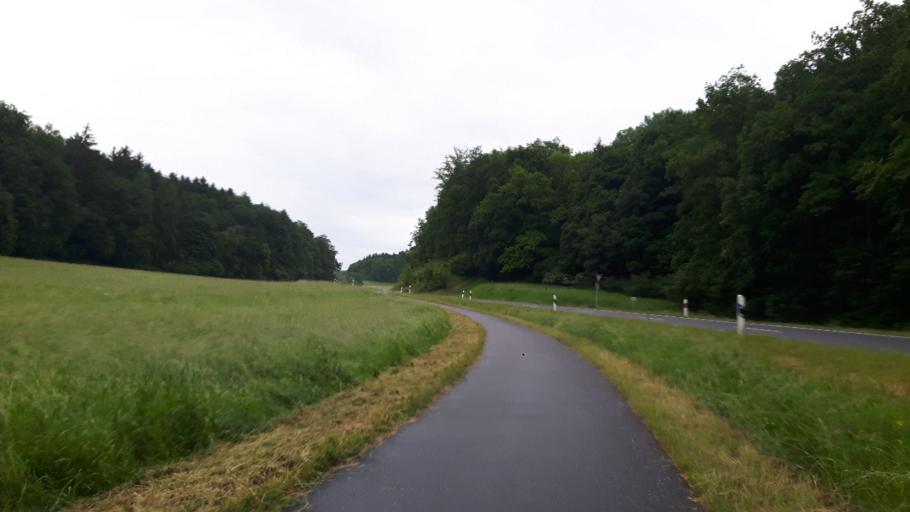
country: DE
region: Bavaria
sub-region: Regierungsbezirk Unterfranken
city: Uchtelhausen
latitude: 50.1035
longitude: 10.2581
